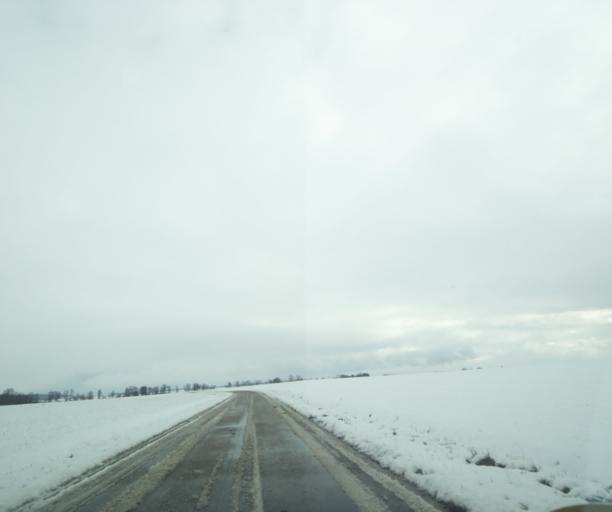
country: FR
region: Champagne-Ardenne
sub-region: Departement de la Haute-Marne
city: Montier-en-Der
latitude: 48.4490
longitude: 4.6991
